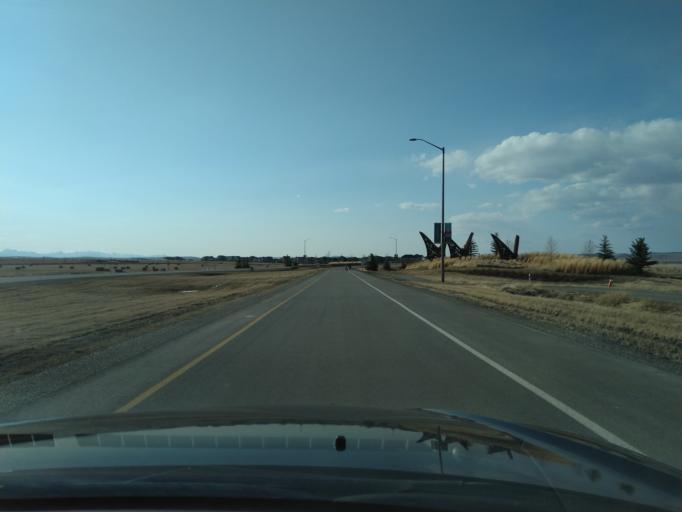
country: CA
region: Alberta
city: Cochrane
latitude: 51.1042
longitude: -114.3899
